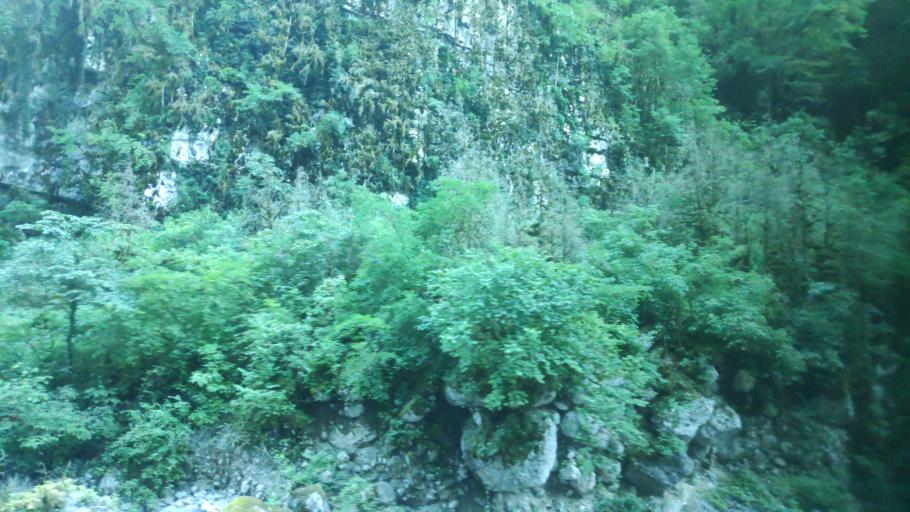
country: GE
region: Abkhazia
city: Gagra
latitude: 43.4376
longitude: 40.5331
